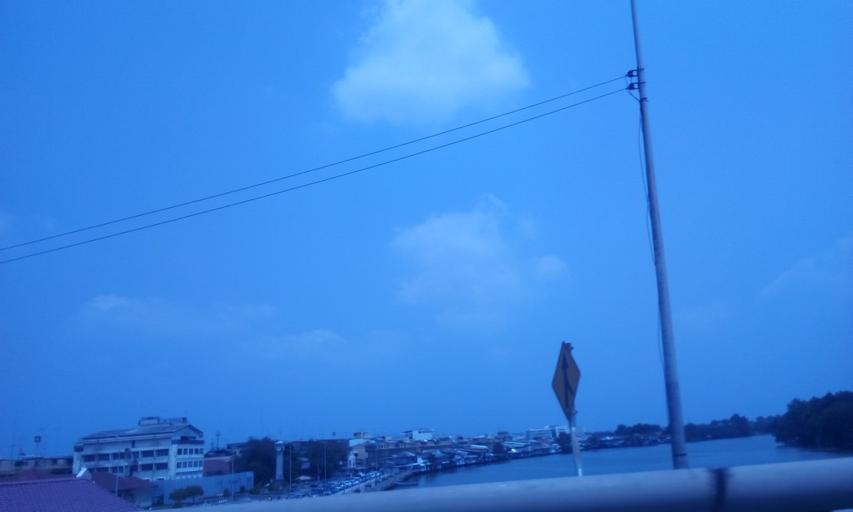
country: TH
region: Chachoengsao
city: Chachoengsao
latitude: 13.6885
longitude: 101.0768
